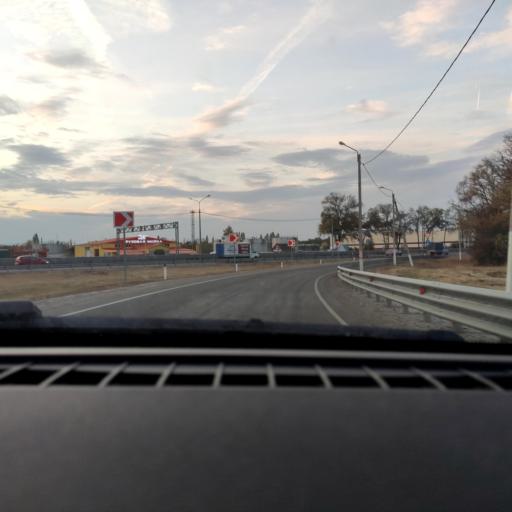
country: RU
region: Voronezj
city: Podgornoye
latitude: 51.8013
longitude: 39.2039
